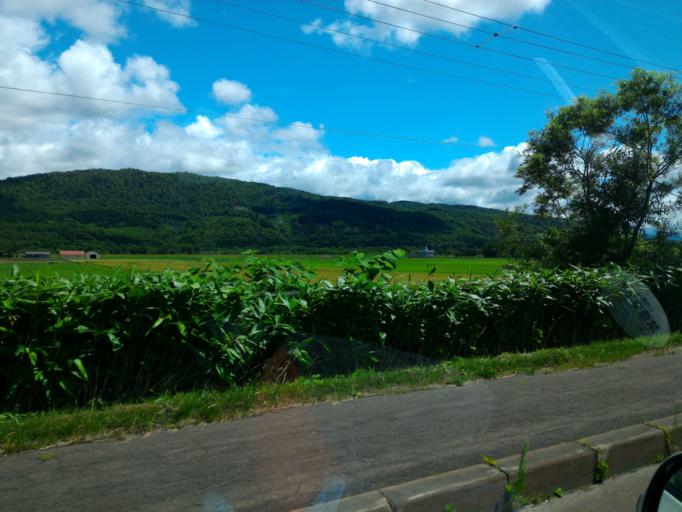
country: JP
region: Hokkaido
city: Nayoro
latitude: 44.5649
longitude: 142.3166
